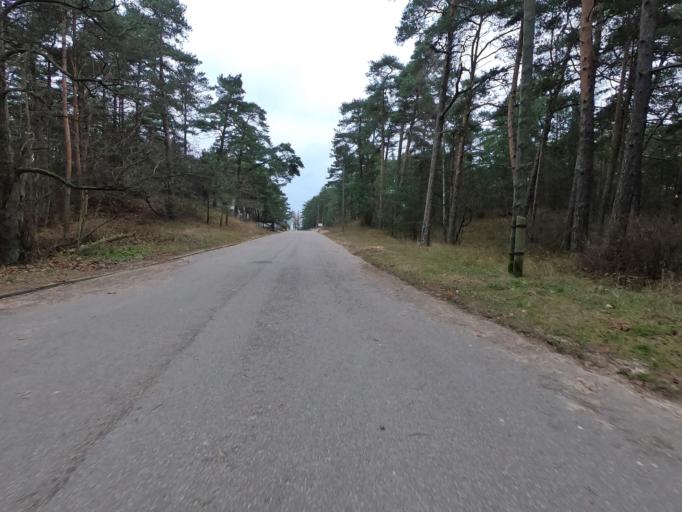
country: LV
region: Riga
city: Bolderaja
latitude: 57.0795
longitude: 24.1090
